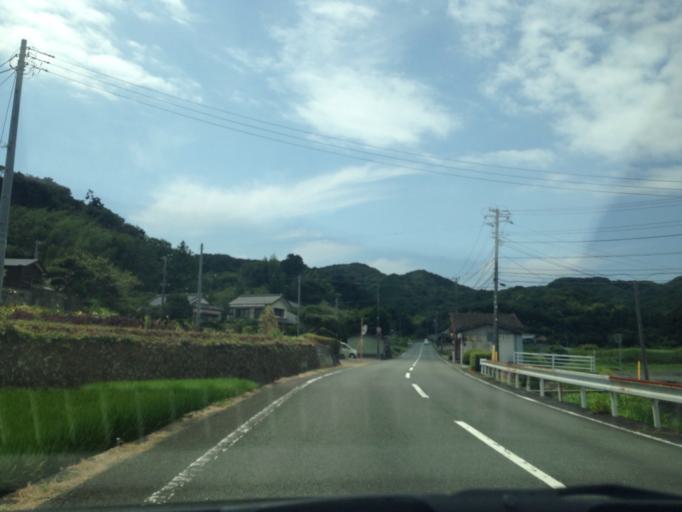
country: JP
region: Shizuoka
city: Shimoda
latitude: 34.6521
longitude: 138.8157
